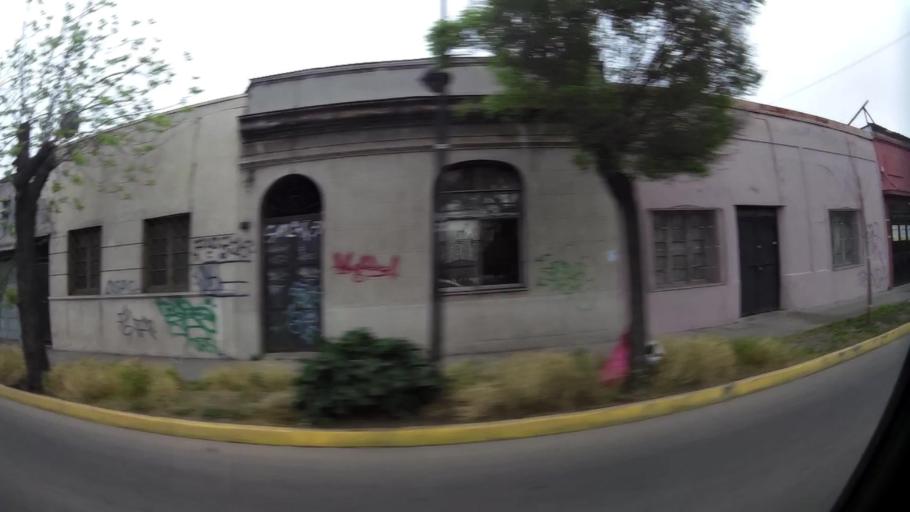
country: CL
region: Santiago Metropolitan
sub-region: Provincia de Santiago
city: Santiago
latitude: -33.4650
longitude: -70.6444
